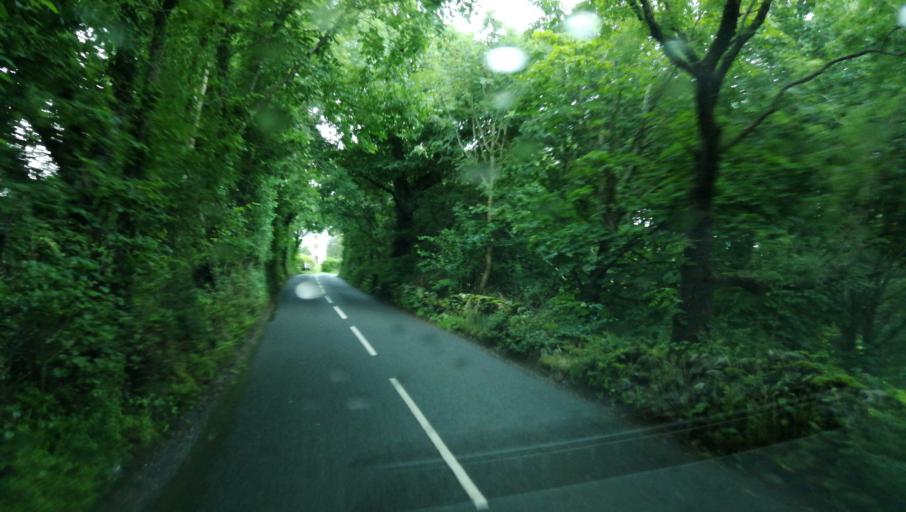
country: GB
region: England
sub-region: Cumbria
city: Penrith
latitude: 54.5922
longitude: -2.8593
